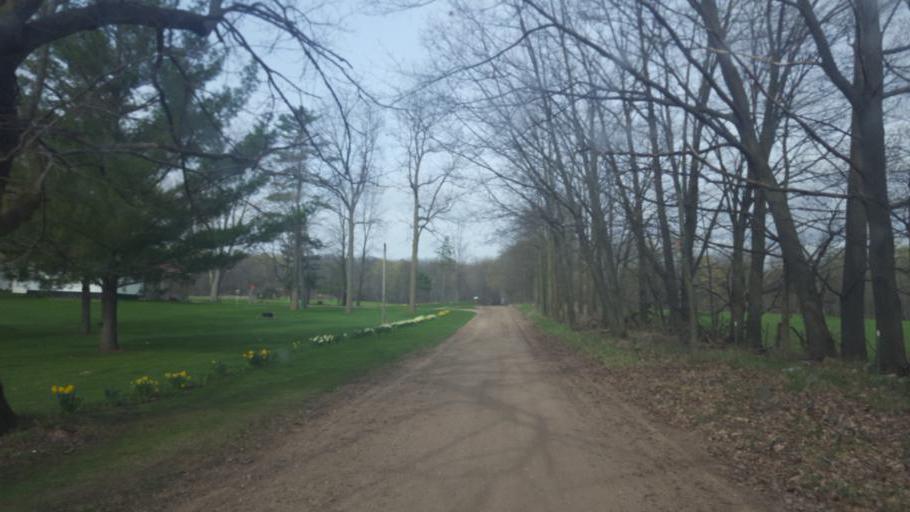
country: US
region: Michigan
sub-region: Isabella County
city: Lake Isabella
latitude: 43.5178
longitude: -84.9315
